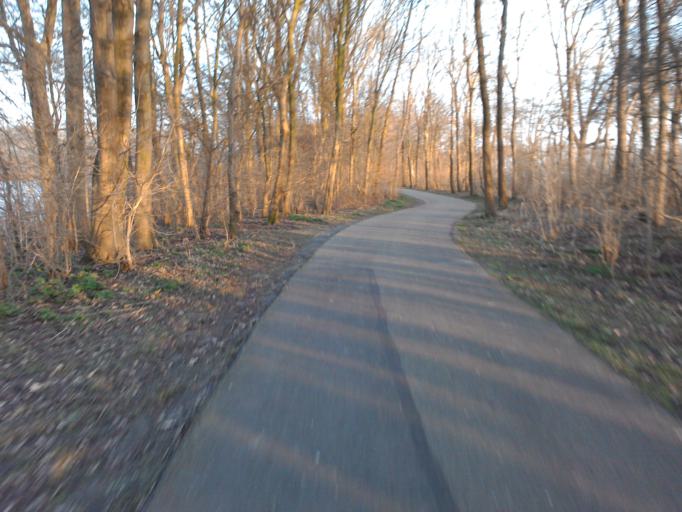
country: NL
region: Utrecht
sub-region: Stichtse Vecht
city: Maarssen
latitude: 52.1370
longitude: 5.0918
